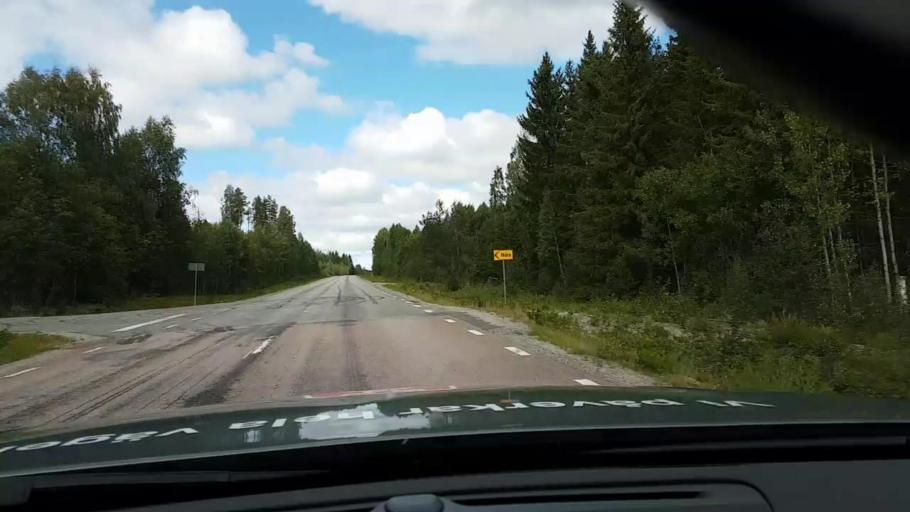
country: SE
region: Vaesternorrland
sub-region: OErnskoeldsviks Kommun
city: Bredbyn
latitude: 63.4702
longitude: 18.1003
